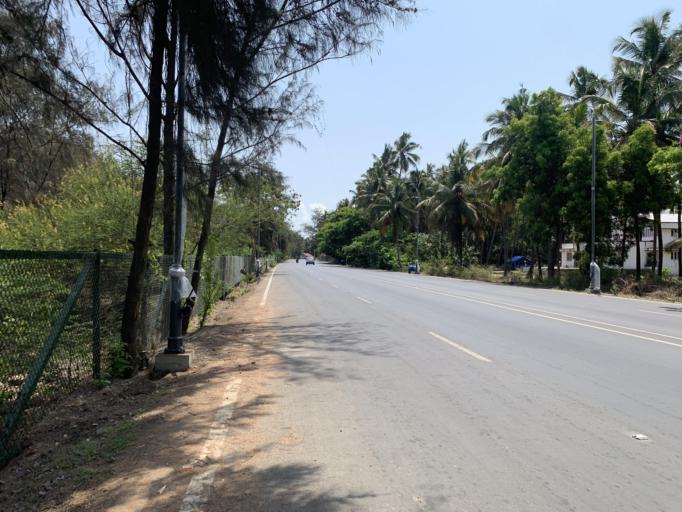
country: IN
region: Daman and Diu
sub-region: Daman District
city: Daman
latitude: 20.4614
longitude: 72.8489
